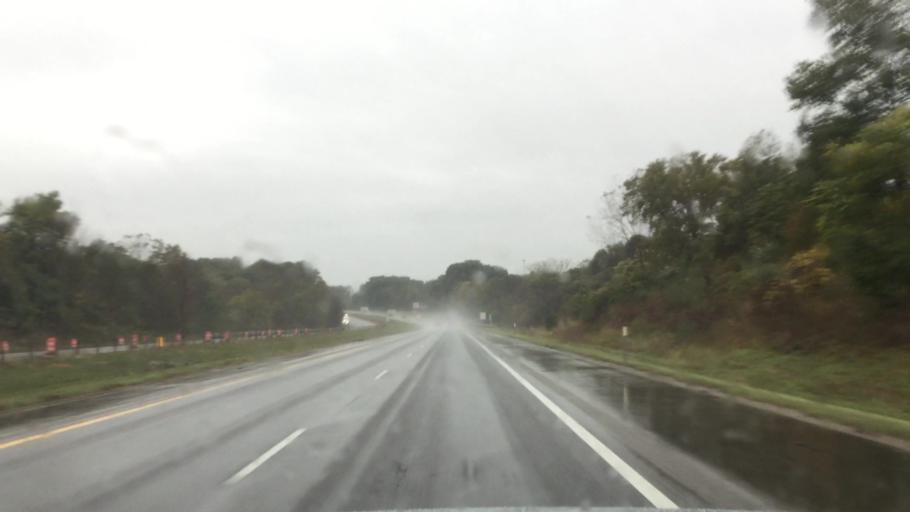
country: US
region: Michigan
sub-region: Van Buren County
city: Hartford
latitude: 42.1976
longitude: -86.0938
